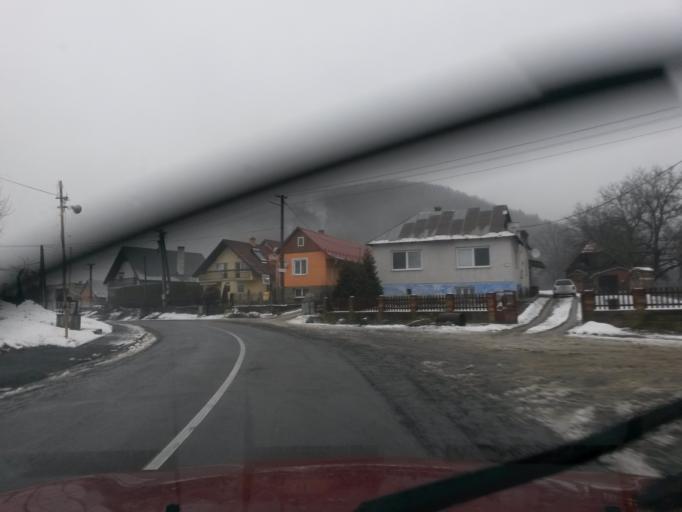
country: SK
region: Presovsky
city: Humenne
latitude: 49.0935
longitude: 21.8276
